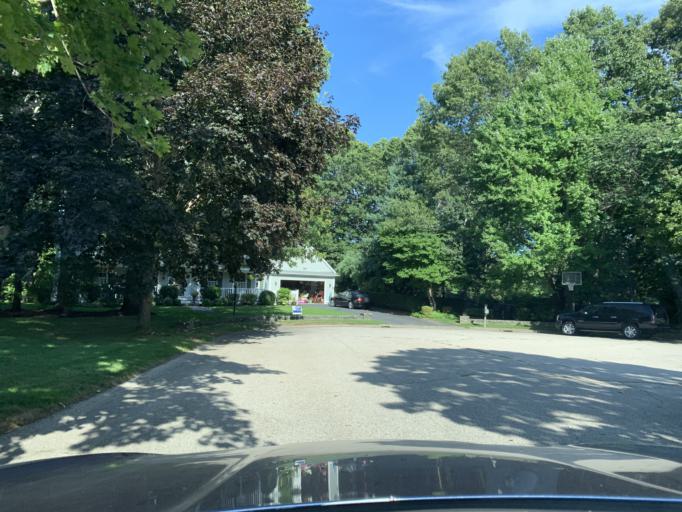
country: US
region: Rhode Island
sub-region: Kent County
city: East Greenwich
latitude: 41.6332
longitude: -71.4560
